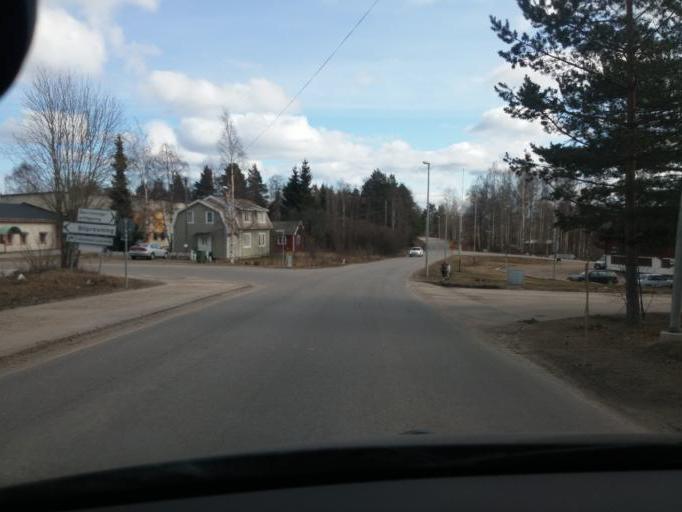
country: SE
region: Gaevleborg
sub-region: Ljusdals Kommun
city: Ljusdal
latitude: 61.8229
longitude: 16.1150
